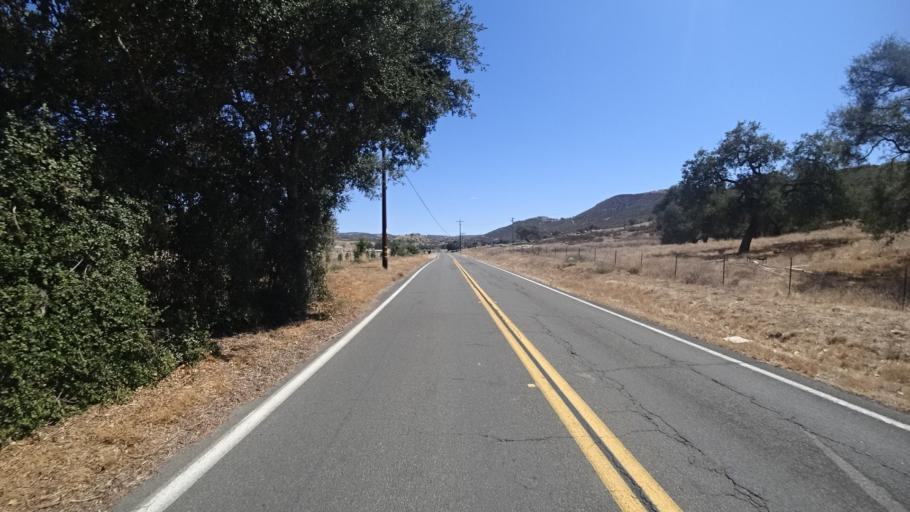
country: US
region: California
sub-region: San Diego County
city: San Diego Country Estates
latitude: 33.0498
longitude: -116.8084
